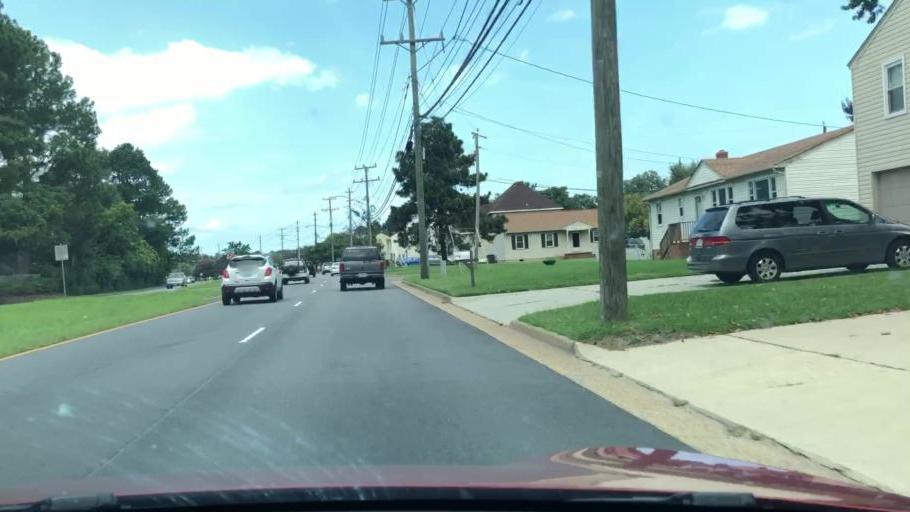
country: US
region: Virginia
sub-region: City of Norfolk
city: Norfolk
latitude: 36.8905
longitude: -76.1385
